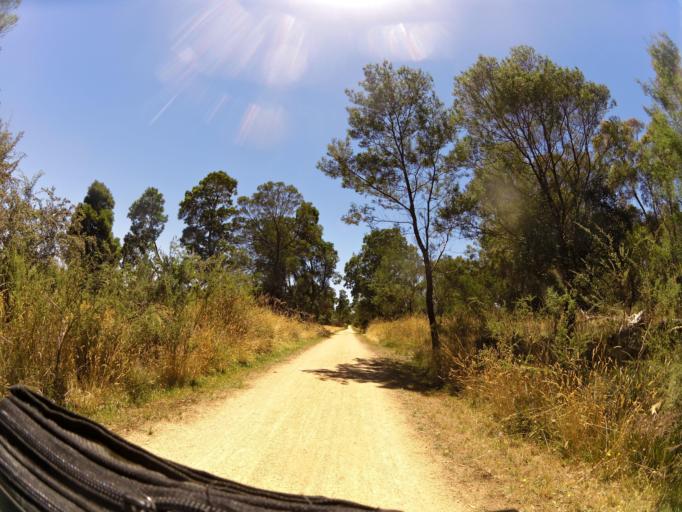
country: AU
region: Victoria
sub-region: Ballarat North
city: Delacombe
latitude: -37.6339
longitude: 143.6937
